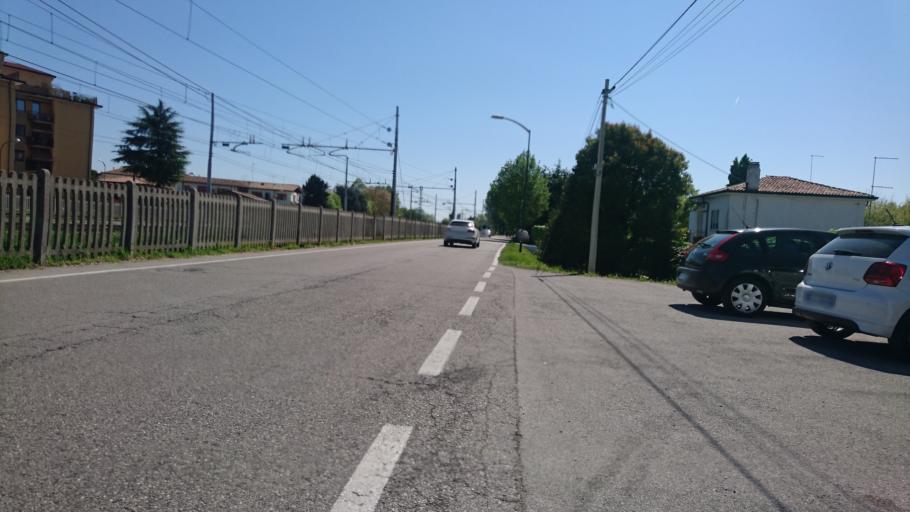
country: IT
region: Veneto
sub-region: Provincia di Treviso
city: Treviso
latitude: 45.6617
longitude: 12.2300
